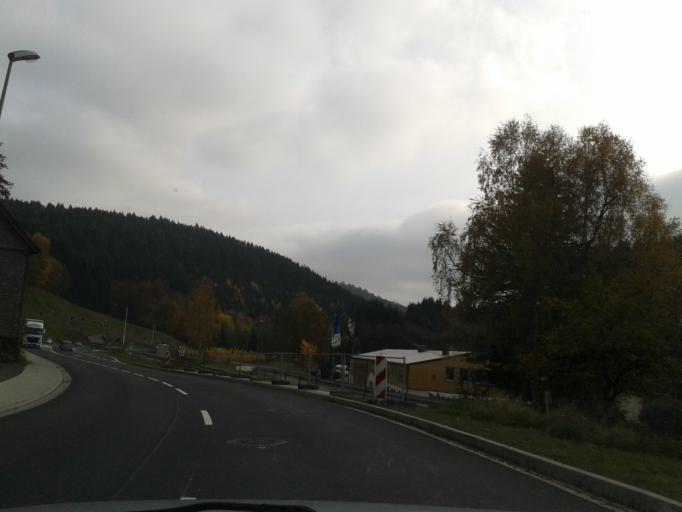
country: DE
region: North Rhine-Westphalia
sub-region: Regierungsbezirk Arnsberg
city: Bad Laasphe
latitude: 50.9499
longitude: 8.3707
